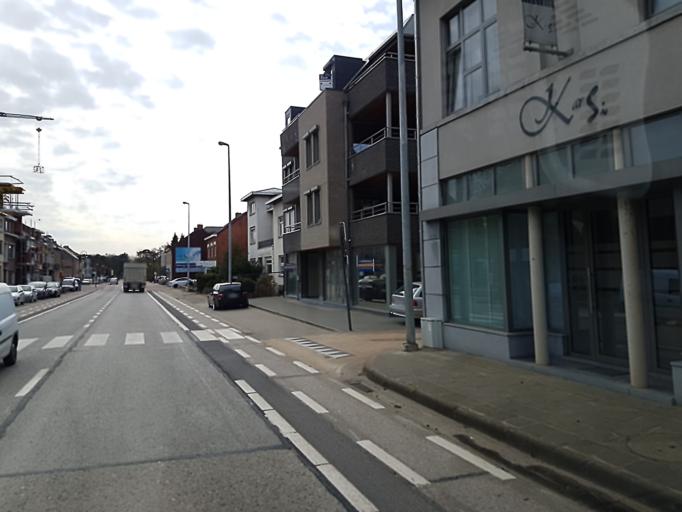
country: BE
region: Flanders
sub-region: Provincie Vlaams-Brabant
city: Scherpenheuvel-Zichem
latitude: 51.0283
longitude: 4.9814
